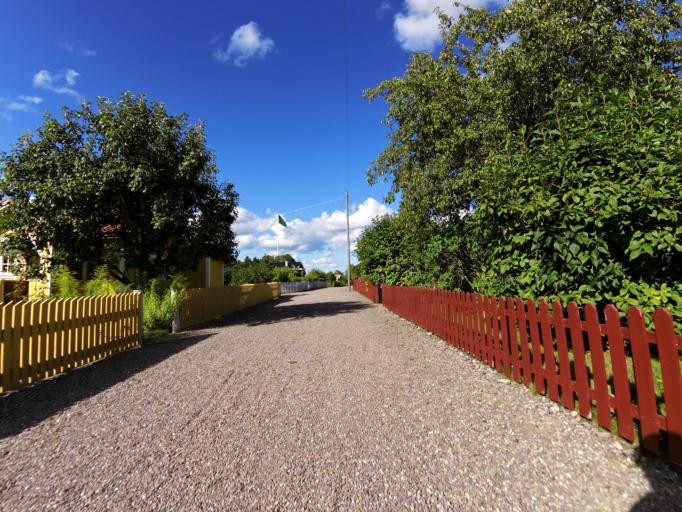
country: SE
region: Gaevleborg
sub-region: Gavle Kommun
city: Gavle
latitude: 60.7070
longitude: 17.1584
